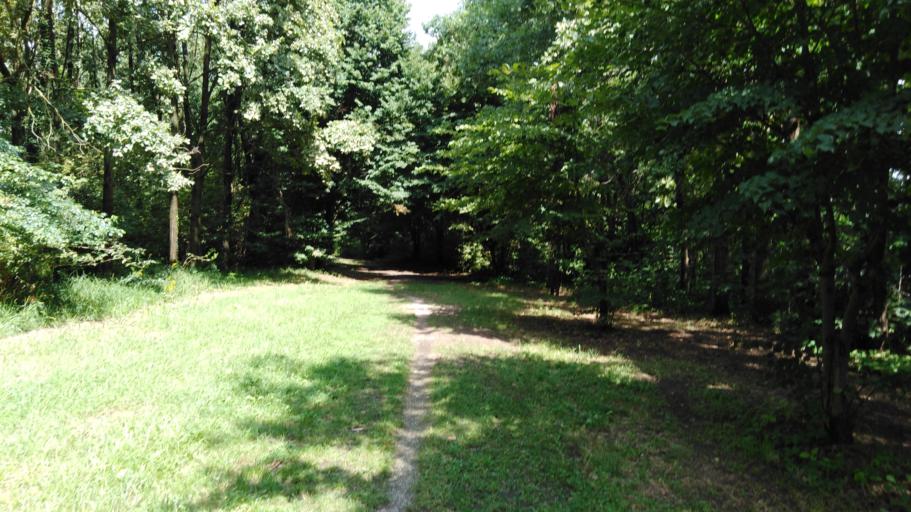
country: HU
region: Zala
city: Zalakomar
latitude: 46.6063
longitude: 17.1669
